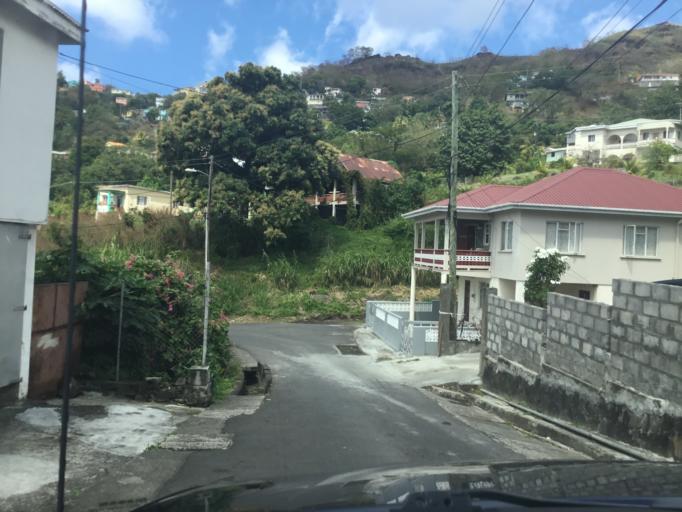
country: VC
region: Saint George
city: Kingstown Park
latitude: 13.1588
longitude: -61.2345
